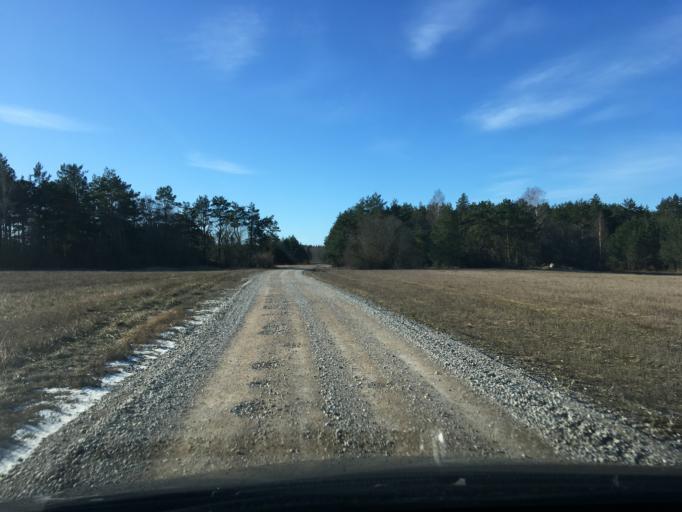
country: EE
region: Laeaene
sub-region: Lihula vald
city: Lihula
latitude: 58.5762
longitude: 23.6996
